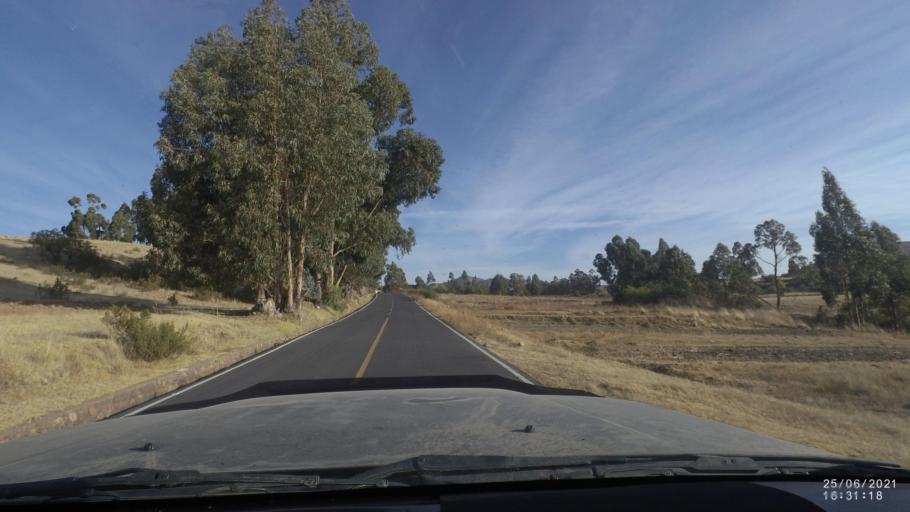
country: BO
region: Cochabamba
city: Arani
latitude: -17.7994
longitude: -65.8015
